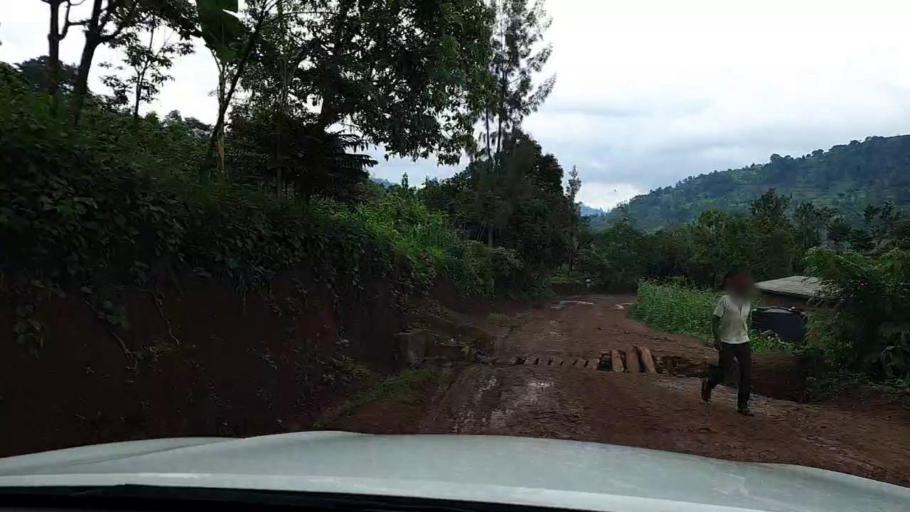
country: RW
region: Western Province
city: Cyangugu
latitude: -2.5667
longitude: 29.0331
